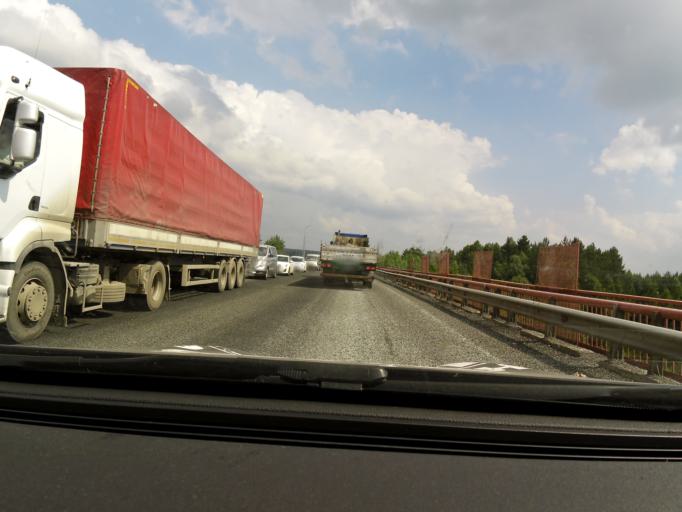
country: RU
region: Sverdlovsk
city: Ufimskiy
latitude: 56.7636
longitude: 58.1428
